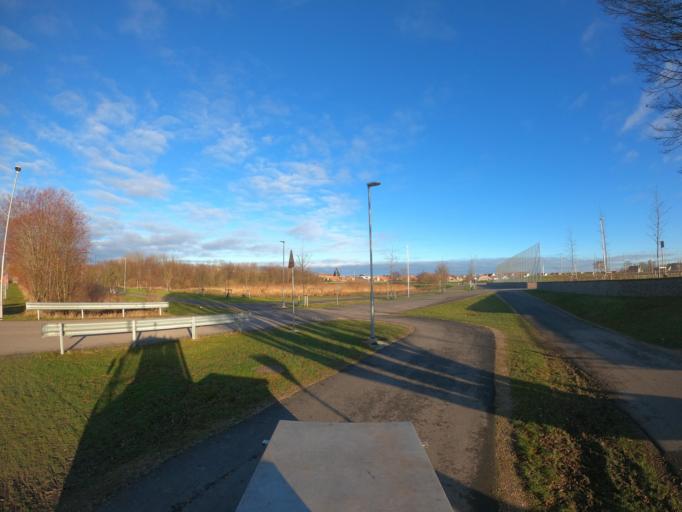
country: SE
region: Skane
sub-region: Svedala Kommun
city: Svedala
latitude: 55.5030
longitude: 13.2361
